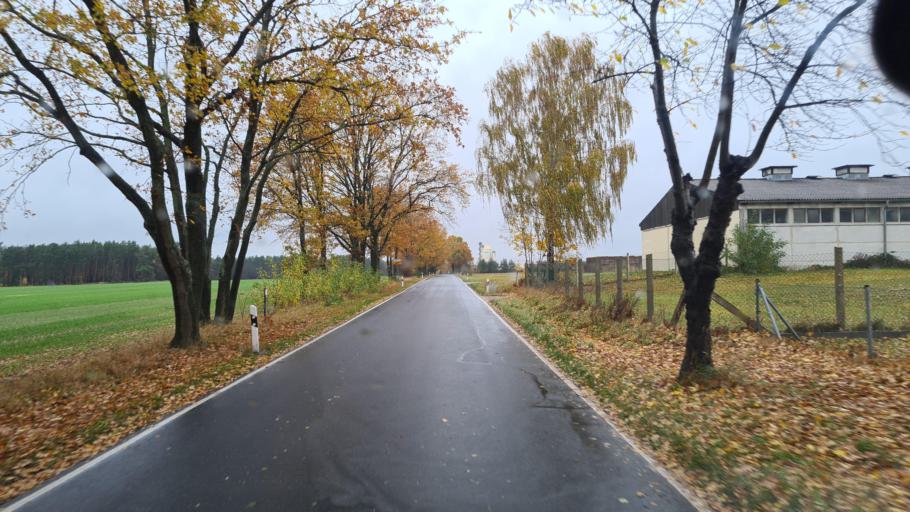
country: DE
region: Brandenburg
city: Drebkau
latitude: 51.6836
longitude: 14.2038
